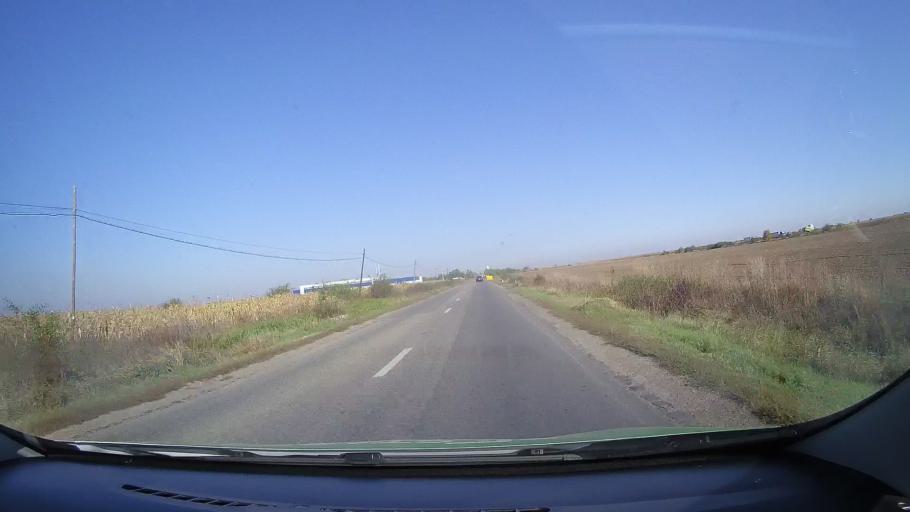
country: RO
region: Satu Mare
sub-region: Oras Tasnad
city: Tasnad
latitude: 47.5023
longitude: 22.5743
